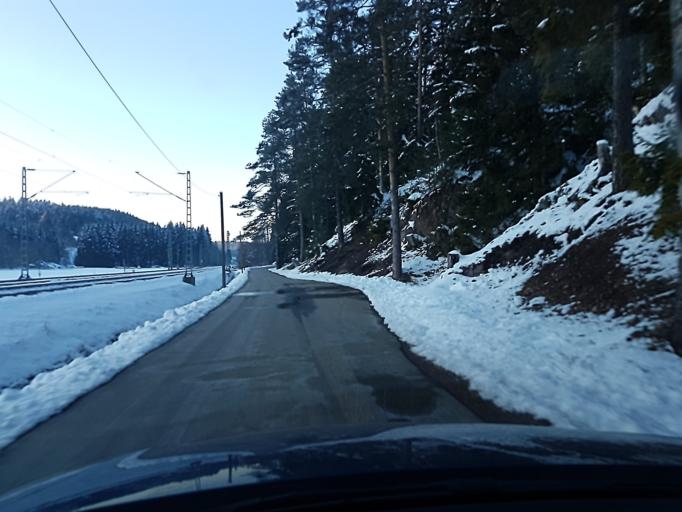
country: DE
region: Baden-Wuerttemberg
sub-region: Freiburg Region
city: Monchweiler
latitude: 48.0913
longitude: 8.4035
